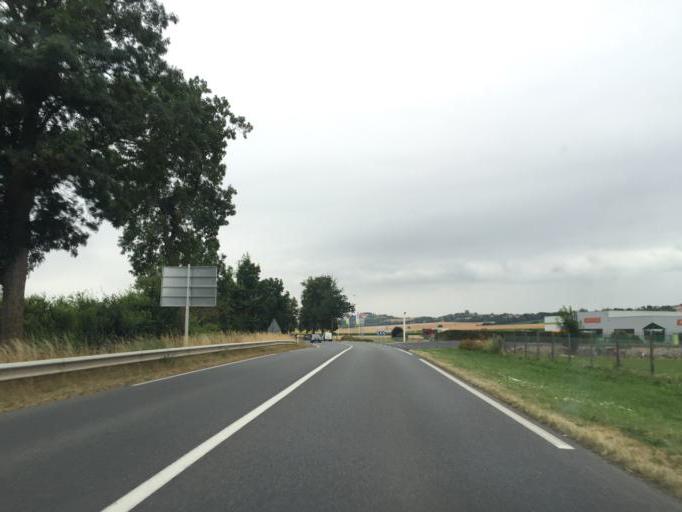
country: FR
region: Auvergne
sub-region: Departement de l'Allier
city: Gannat
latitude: 46.1373
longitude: 3.2125
